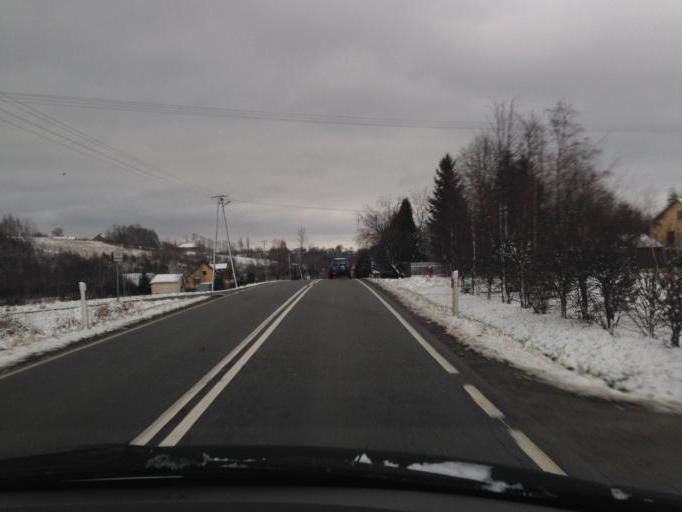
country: PL
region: Lesser Poland Voivodeship
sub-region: Powiat tarnowski
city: Siemiechow
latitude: 49.8500
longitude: 20.9251
